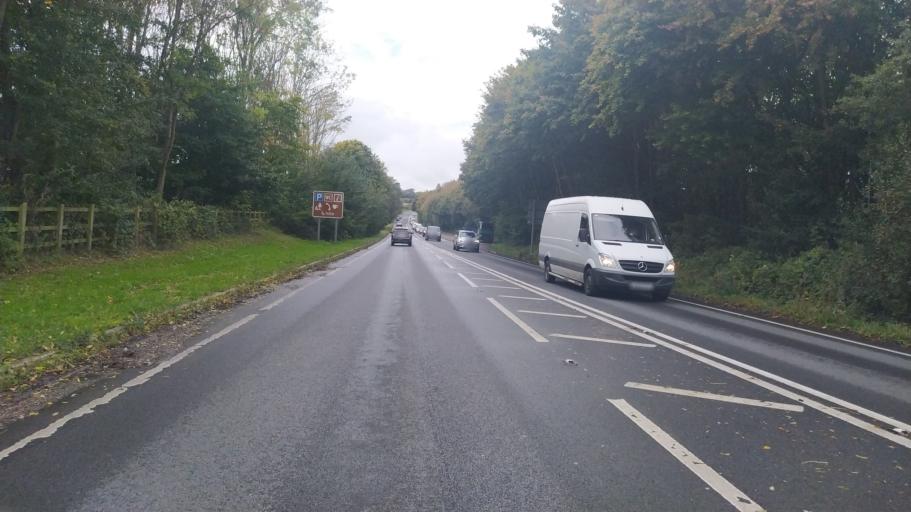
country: GB
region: England
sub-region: Dorset
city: Bridport
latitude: 50.7233
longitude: -2.7644
